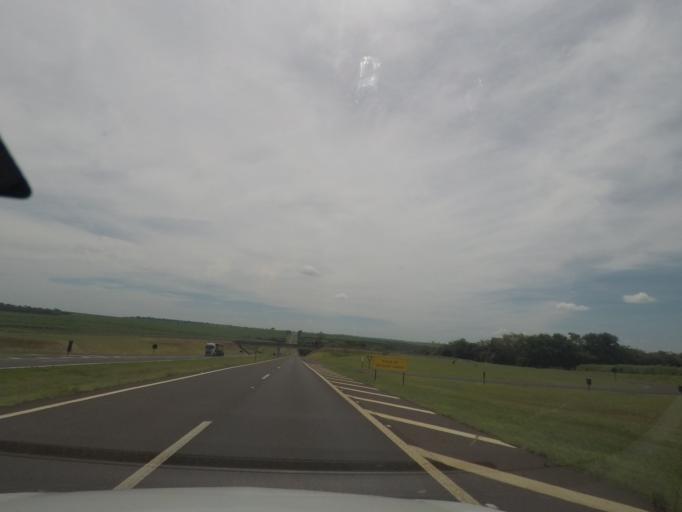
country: BR
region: Sao Paulo
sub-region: Bebedouro
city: Bebedouro
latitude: -21.0404
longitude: -48.4174
